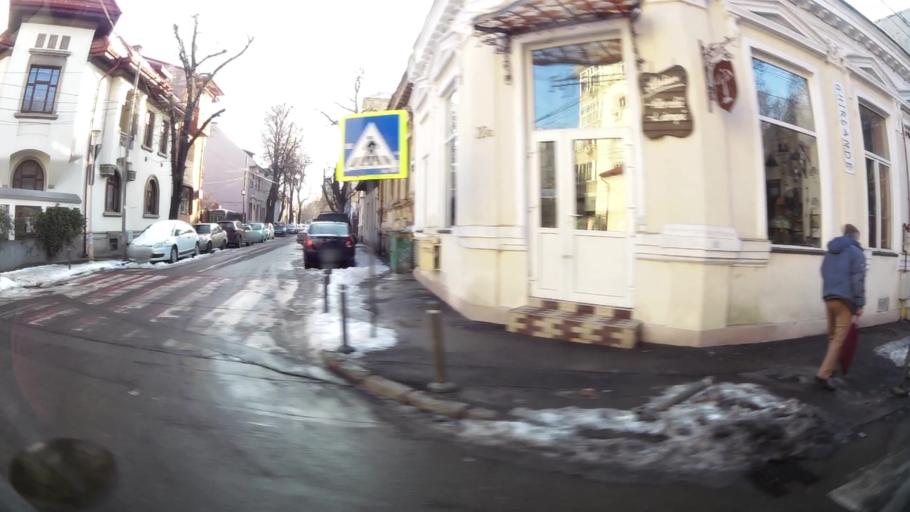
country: RO
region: Bucuresti
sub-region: Municipiul Bucuresti
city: Bucharest
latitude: 44.4385
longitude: 26.1253
